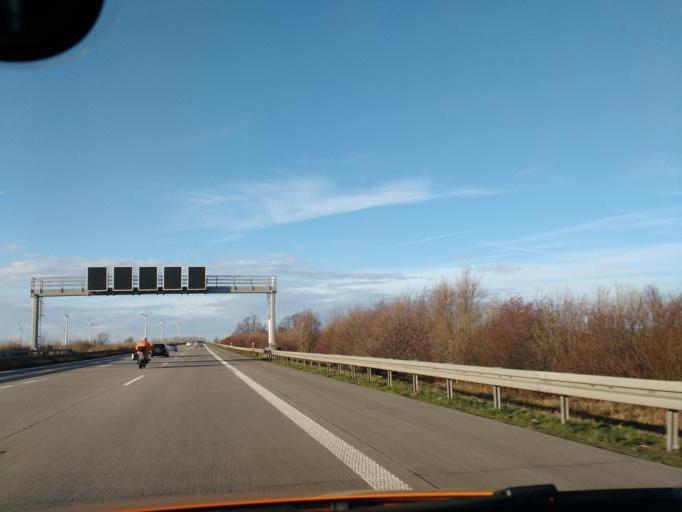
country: DE
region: Saxony-Anhalt
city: Erxleben
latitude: 52.1912
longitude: 11.3090
